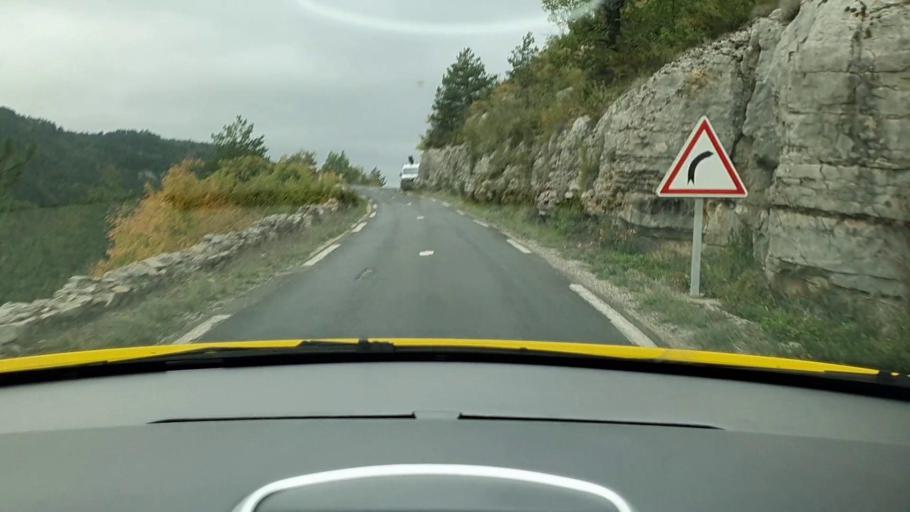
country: FR
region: Languedoc-Roussillon
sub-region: Departement de la Lozere
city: Meyrueis
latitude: 44.0790
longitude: 3.3615
